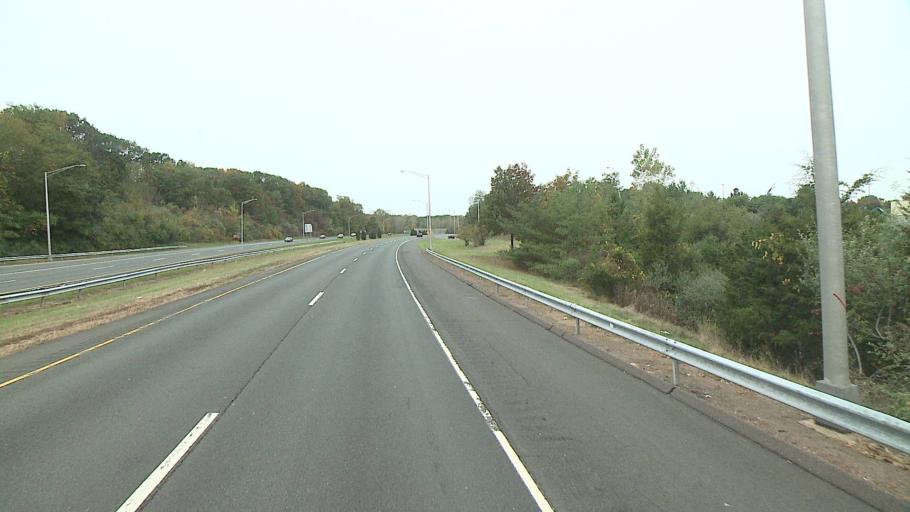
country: US
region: Connecticut
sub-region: Hartford County
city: Newington
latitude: 41.7141
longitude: -72.7663
